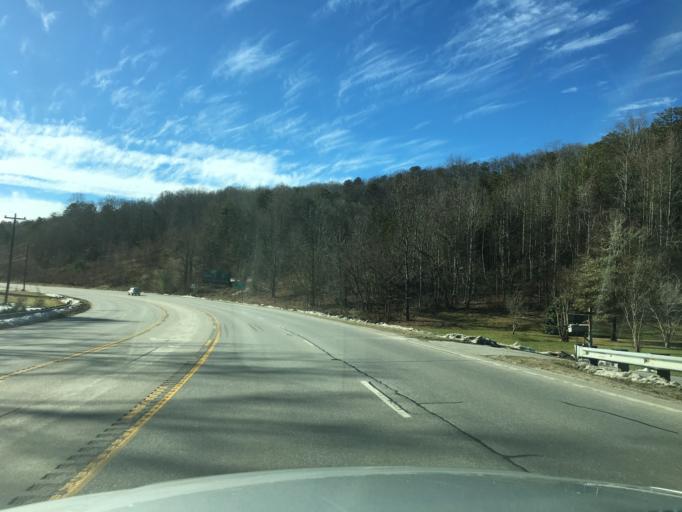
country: US
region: North Carolina
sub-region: Henderson County
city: Etowah
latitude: 35.3291
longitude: -82.6469
